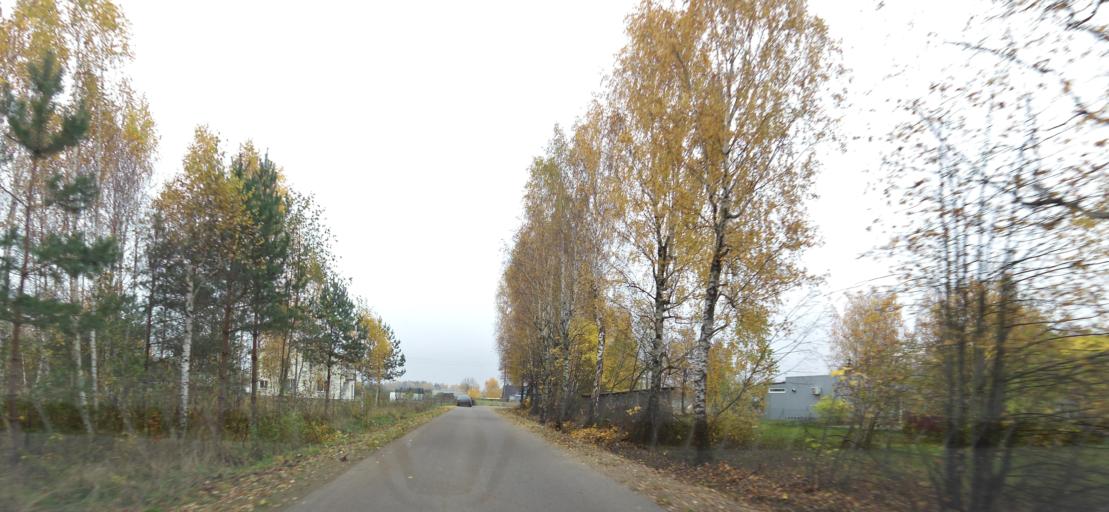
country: LT
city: Skaidiskes
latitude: 54.6457
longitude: 25.6243
